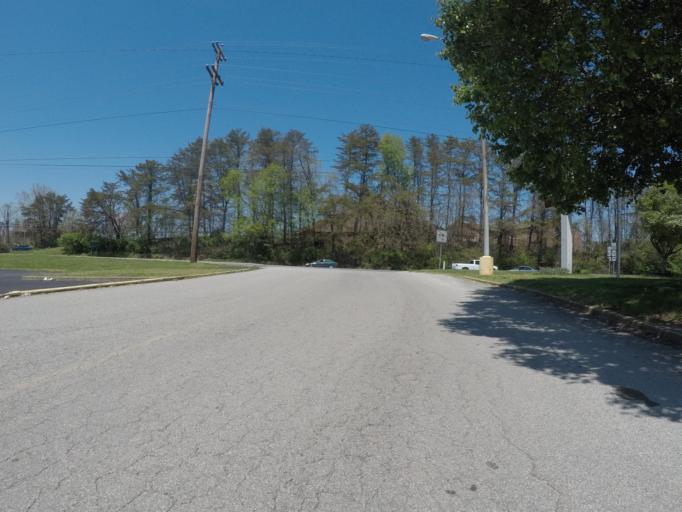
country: US
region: West Virginia
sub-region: Cabell County
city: Pea Ridge
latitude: 38.4108
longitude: -82.3236
